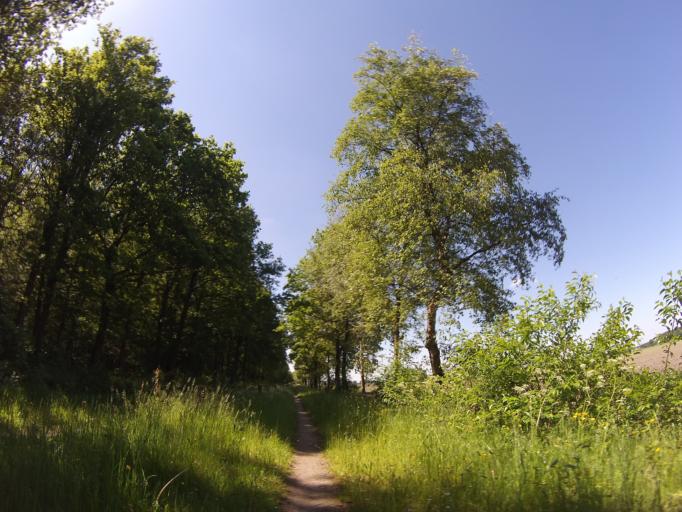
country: NL
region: Drenthe
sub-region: Gemeente Coevorden
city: Dalen
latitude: 52.7666
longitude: 6.6301
